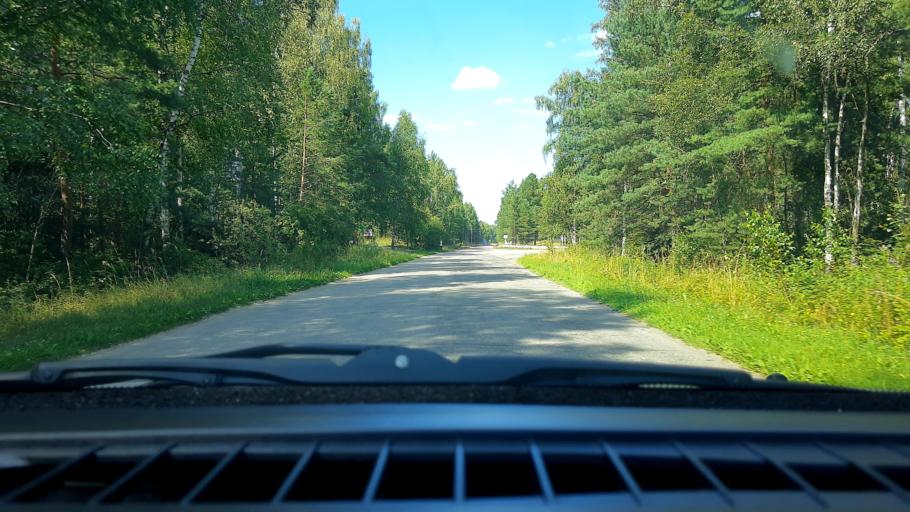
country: RU
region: Nizjnij Novgorod
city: Babino
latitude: 56.3294
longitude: 43.6342
